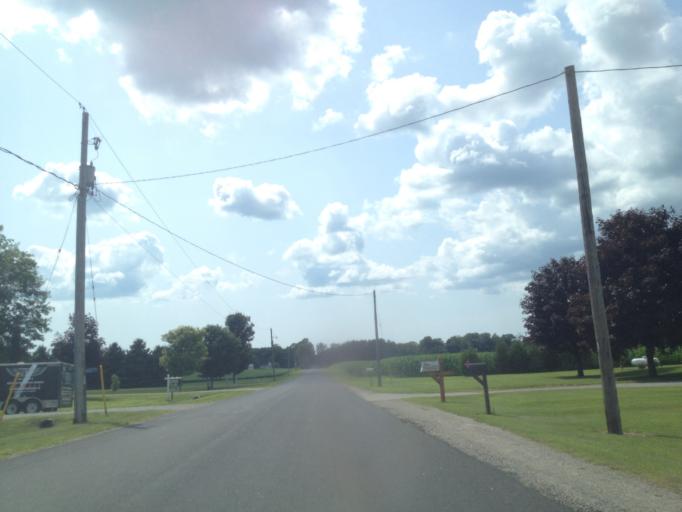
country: CA
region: Ontario
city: Aylmer
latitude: 42.6809
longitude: -80.9895
